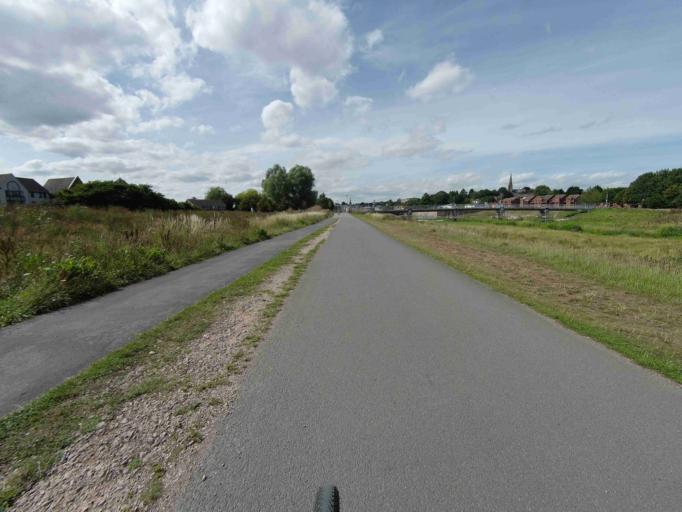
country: GB
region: England
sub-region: Devon
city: Exeter
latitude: 50.7121
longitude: -3.5249
